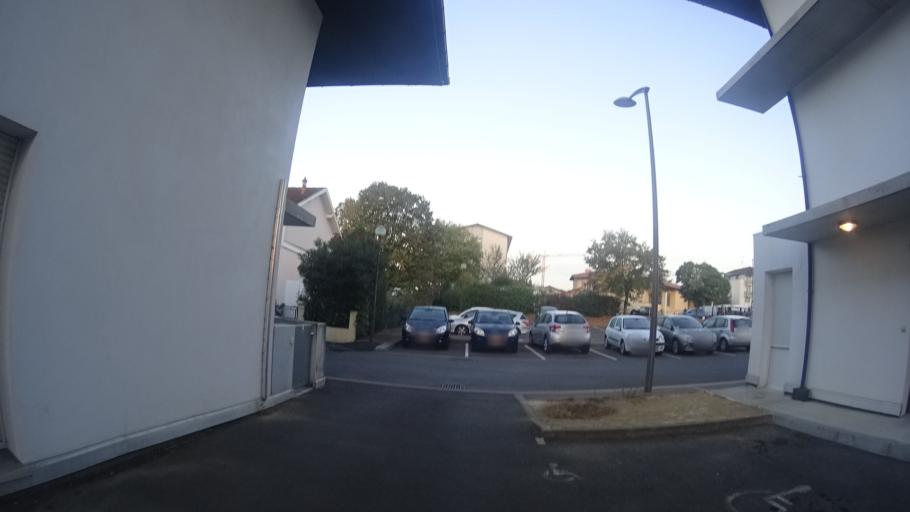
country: FR
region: Aquitaine
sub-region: Departement des Landes
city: Saint-Paul-les-Dax
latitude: 43.7228
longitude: -1.0530
